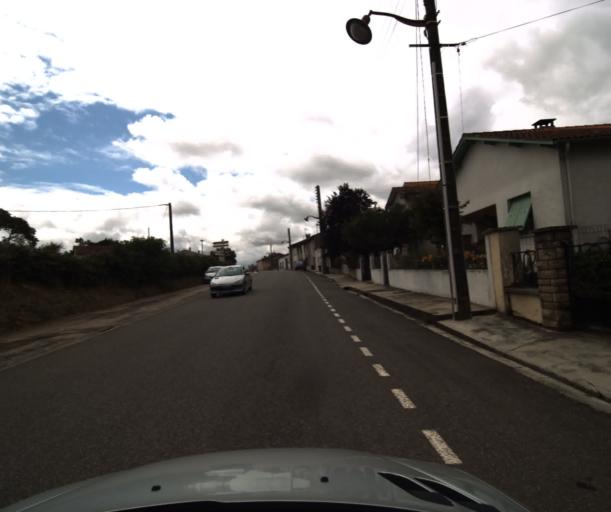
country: FR
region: Midi-Pyrenees
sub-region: Departement du Tarn-et-Garonne
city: Lavit
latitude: 43.9578
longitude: 0.9173
